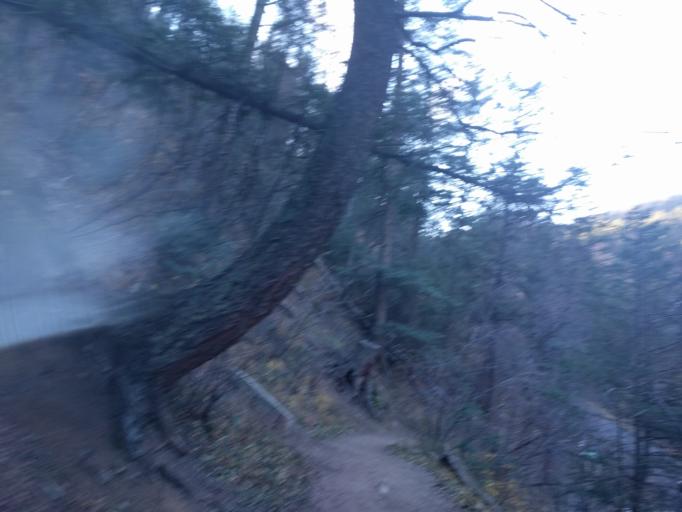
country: US
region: Colorado
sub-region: El Paso County
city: Manitou Springs
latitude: 38.7918
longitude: -104.8868
